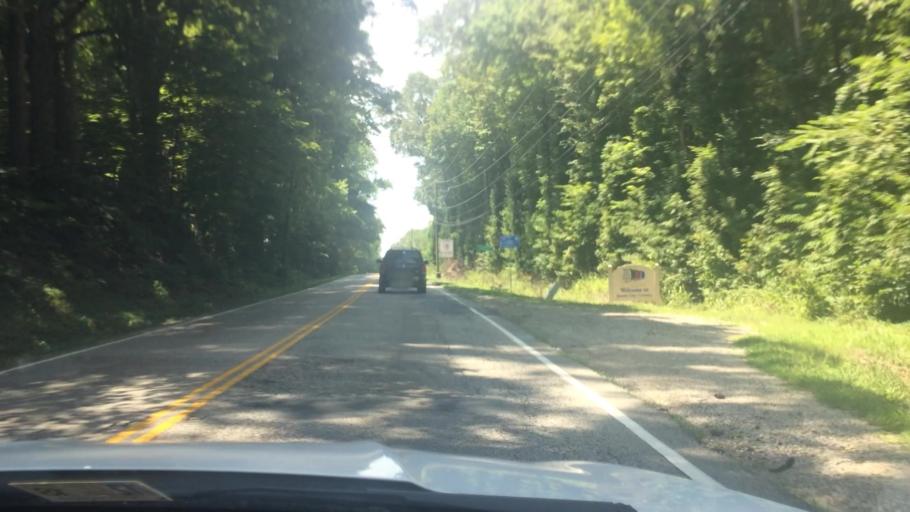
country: US
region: Virginia
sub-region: York County
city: Yorktown
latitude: 37.2091
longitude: -76.5931
